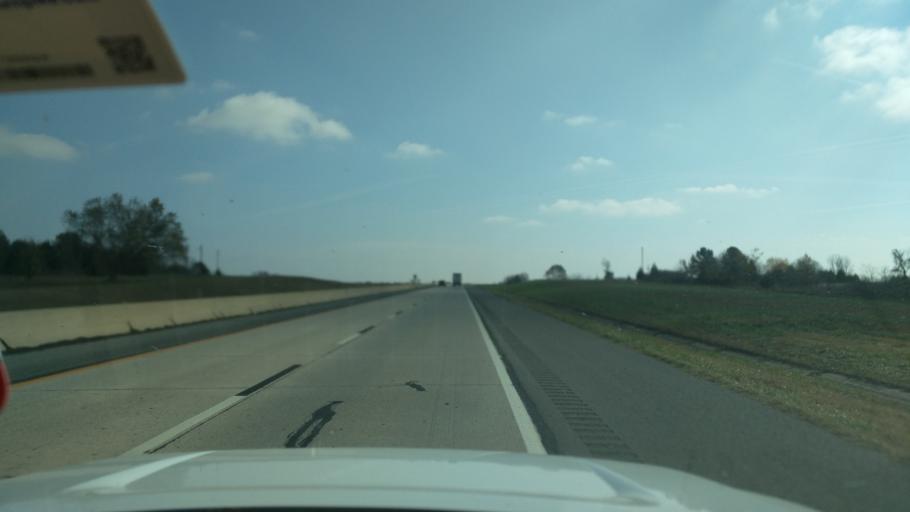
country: US
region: Oklahoma
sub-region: Wagoner County
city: Wagoner
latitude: 35.8861
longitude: -95.4941
